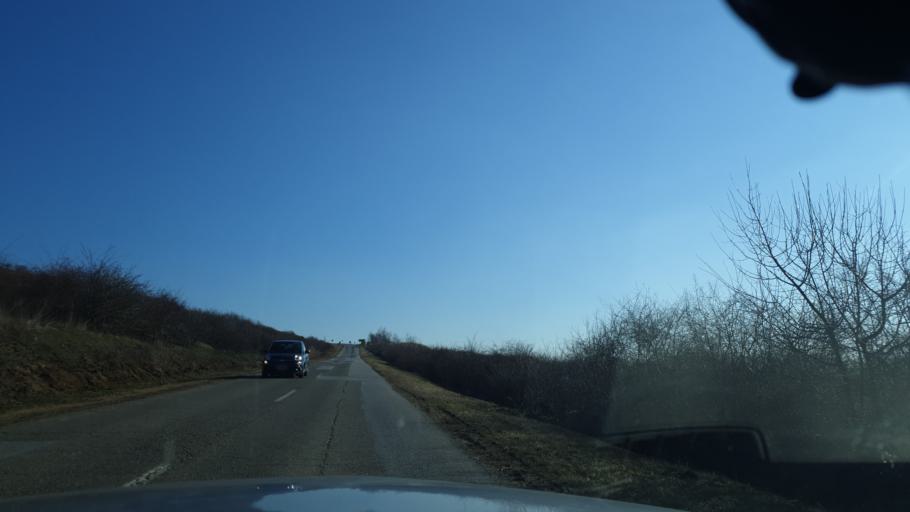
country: RS
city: Vrdnik
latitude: 45.1012
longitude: 19.8036
